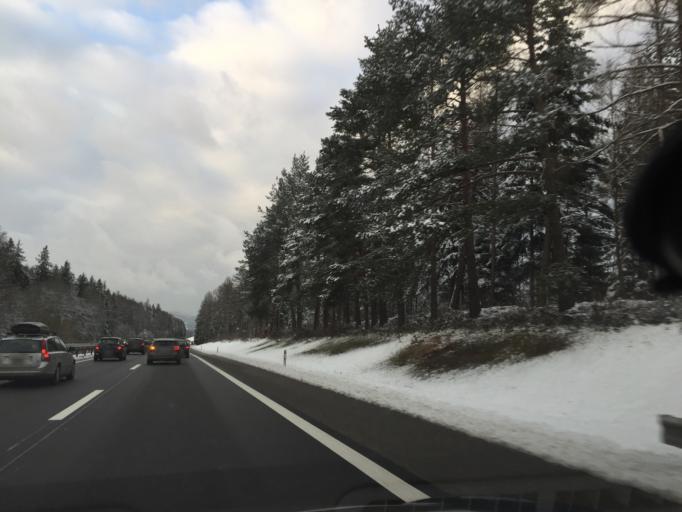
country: CH
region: Zurich
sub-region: Bezirk Horgen
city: Oberrieden / Berg
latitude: 47.2758
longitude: 8.5659
